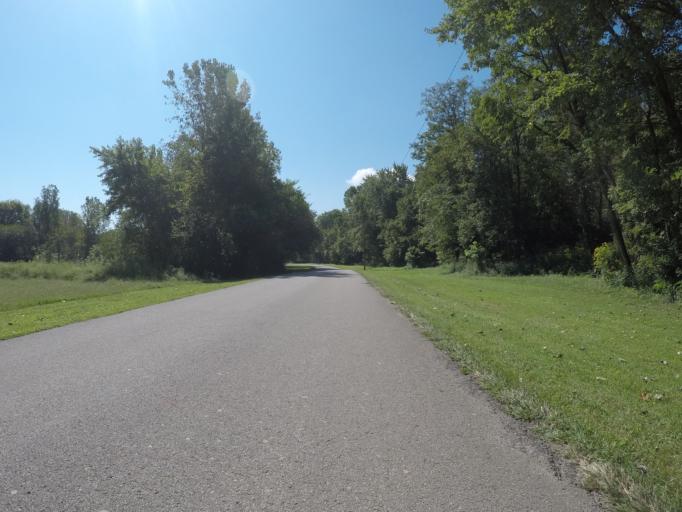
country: US
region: Kentucky
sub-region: Boyd County
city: Catlettsburg
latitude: 38.4114
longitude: -82.5939
